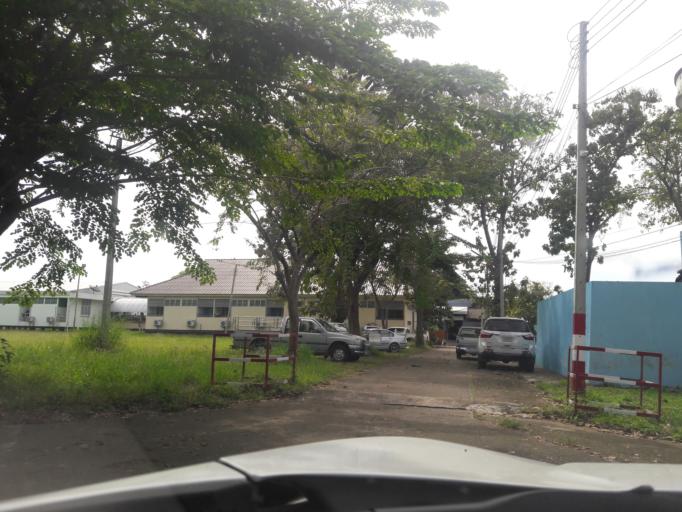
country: TH
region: Nakhon Sawan
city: Tak Fa
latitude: 15.3479
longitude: 100.4923
